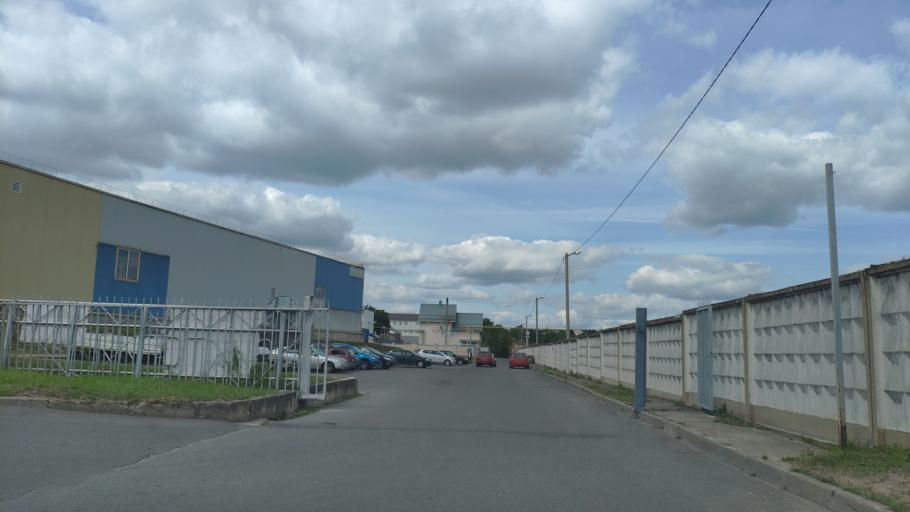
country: BY
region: Minsk
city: Vyaliki Trastsyanets
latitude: 53.8634
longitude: 27.7028
